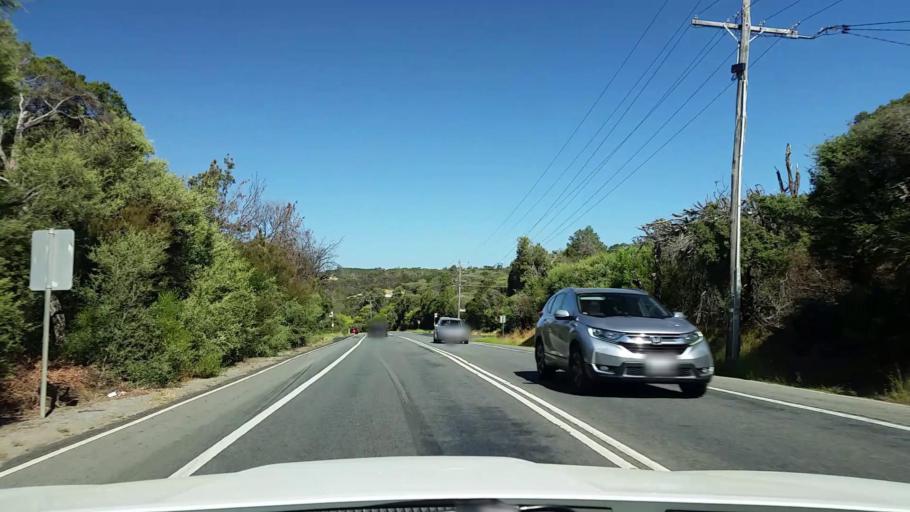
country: AU
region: Victoria
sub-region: Mornington Peninsula
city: Mount Martha
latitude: -38.2599
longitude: 145.0353
